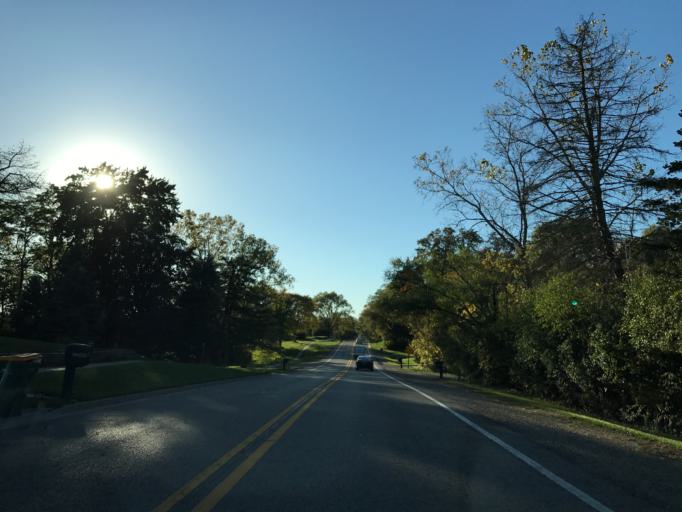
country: US
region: Michigan
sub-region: Oakland County
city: Farmington Hills
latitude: 42.4845
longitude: -83.3638
